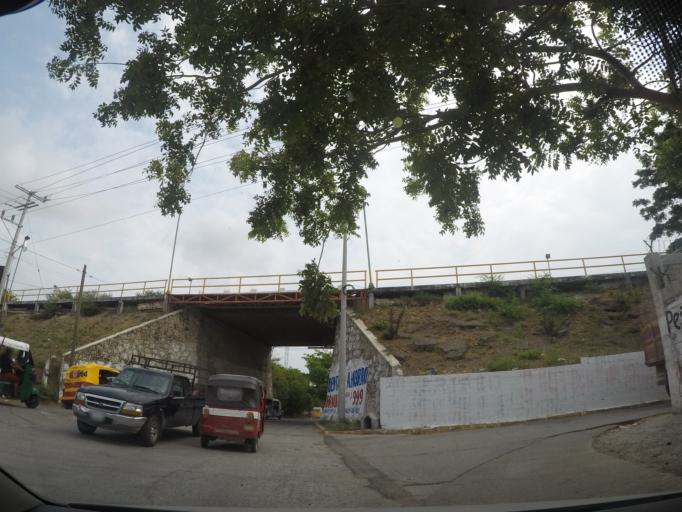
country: MX
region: Oaxaca
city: Juchitan de Zaragoza
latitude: 16.4466
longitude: -95.0215
